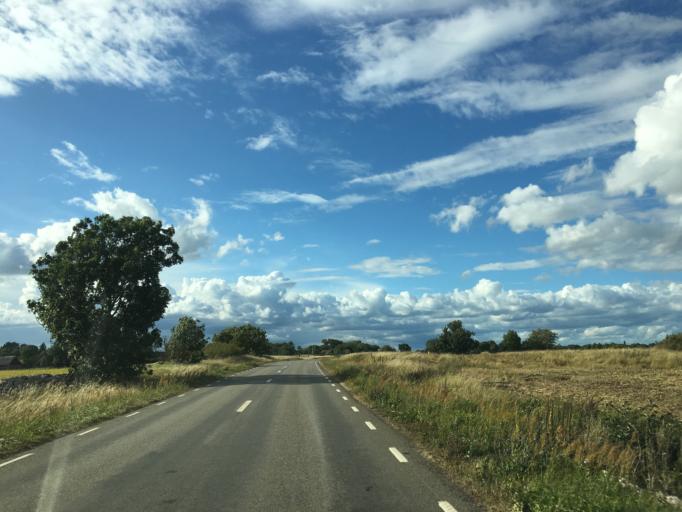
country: SE
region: Kalmar
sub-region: Morbylanga Kommun
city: Moerbylanga
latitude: 56.4397
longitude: 16.4303
